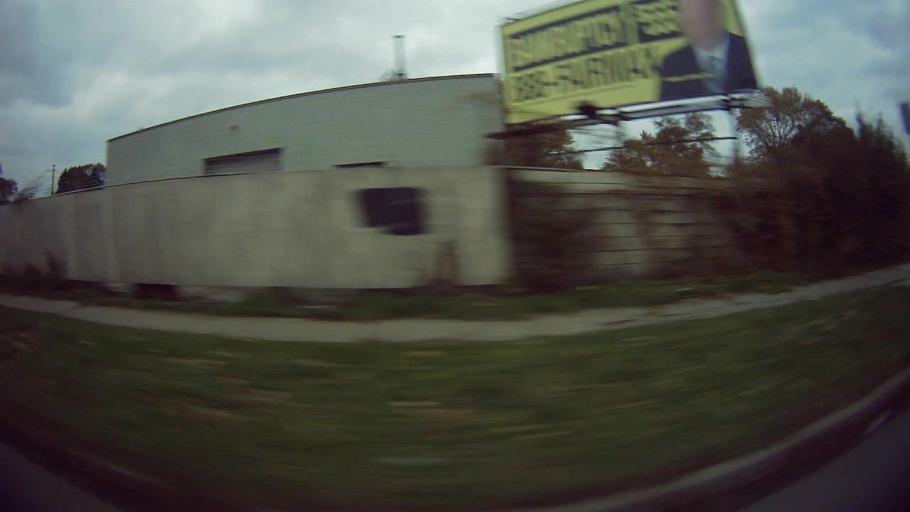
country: US
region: Michigan
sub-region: Wayne County
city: Hamtramck
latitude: 42.4009
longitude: -82.9929
